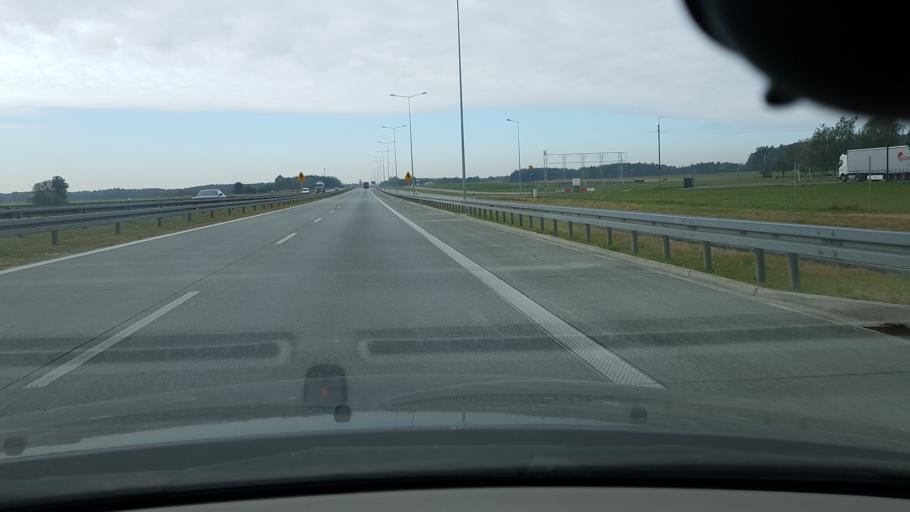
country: PL
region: Lodz Voivodeship
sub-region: Powiat tomaszowski
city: Czerniewice
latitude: 51.6717
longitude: 20.1797
